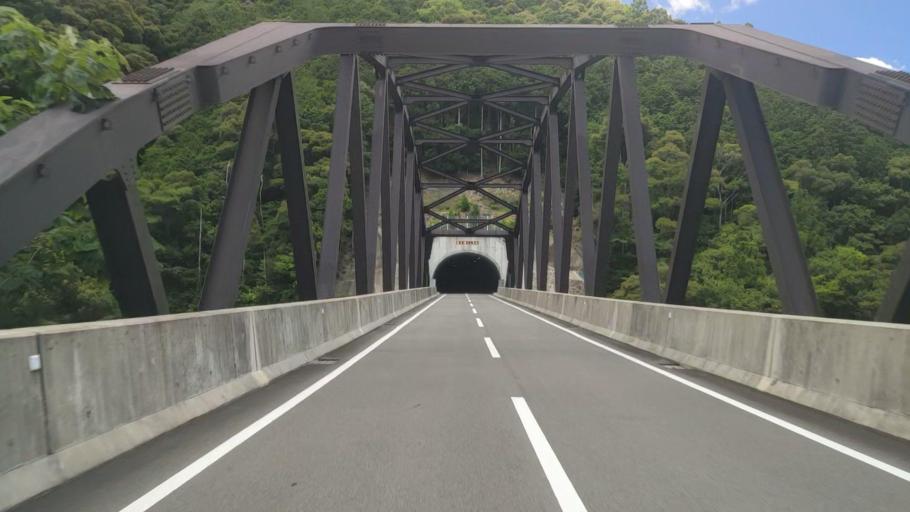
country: JP
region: Mie
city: Owase
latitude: 34.0027
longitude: 136.0093
